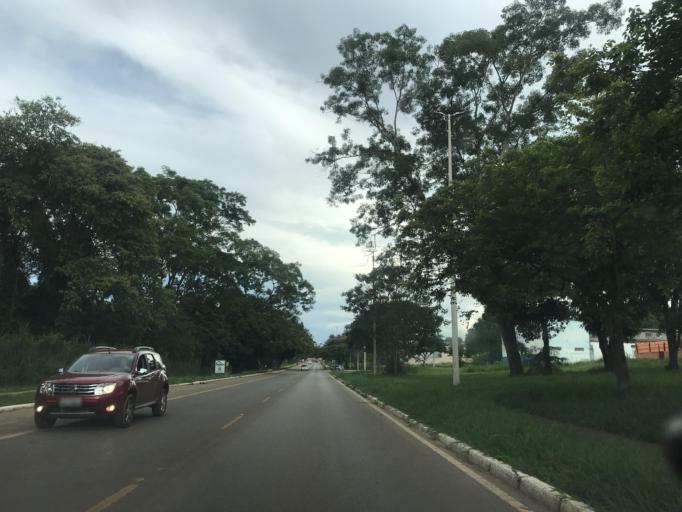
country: BR
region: Federal District
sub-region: Brasilia
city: Brasilia
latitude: -15.6403
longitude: -47.7937
